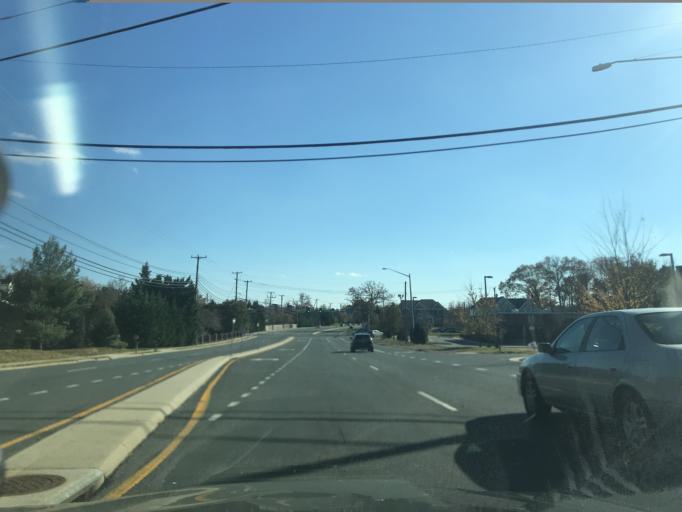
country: US
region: Virginia
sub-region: Fairfax County
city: Greenbriar
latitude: 38.8901
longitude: -77.3784
